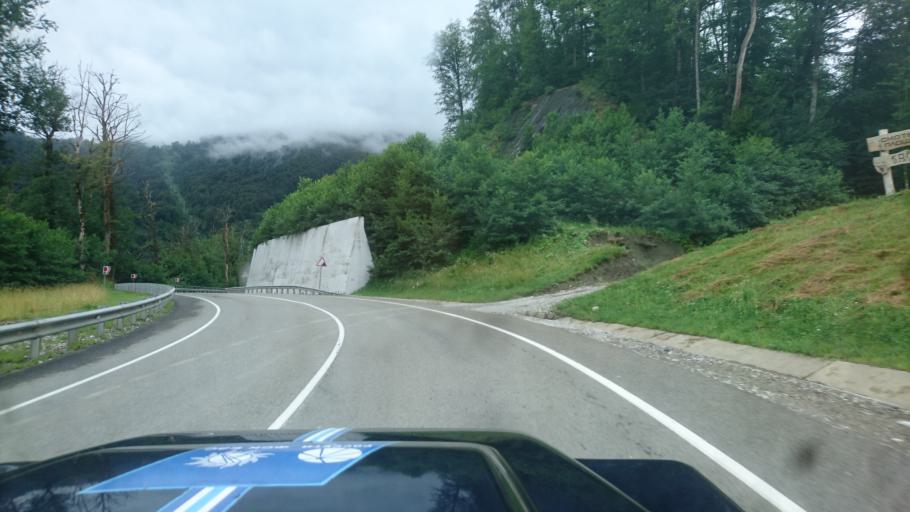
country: RU
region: Krasnodarskiy
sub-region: Sochi City
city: Krasnaya Polyana
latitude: 43.6663
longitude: 40.2997
